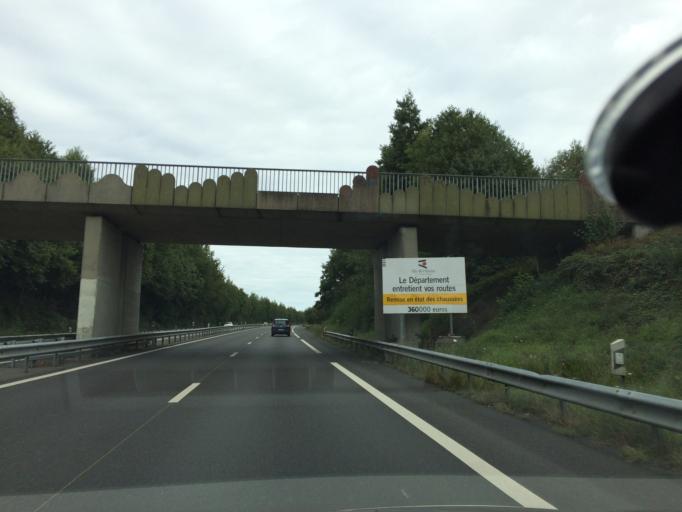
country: FR
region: Brittany
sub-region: Departement d'Ille-et-Vilaine
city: Tinteniac
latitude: 48.3355
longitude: -1.8600
